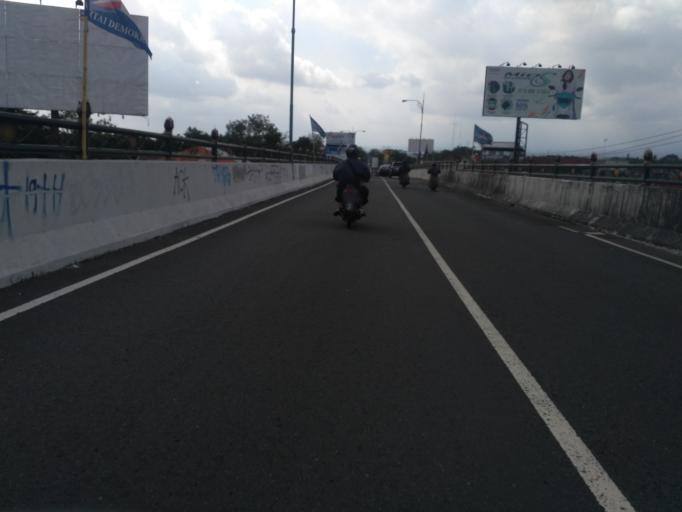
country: ID
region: Daerah Istimewa Yogyakarta
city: Melati
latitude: -7.7477
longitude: 110.3625
